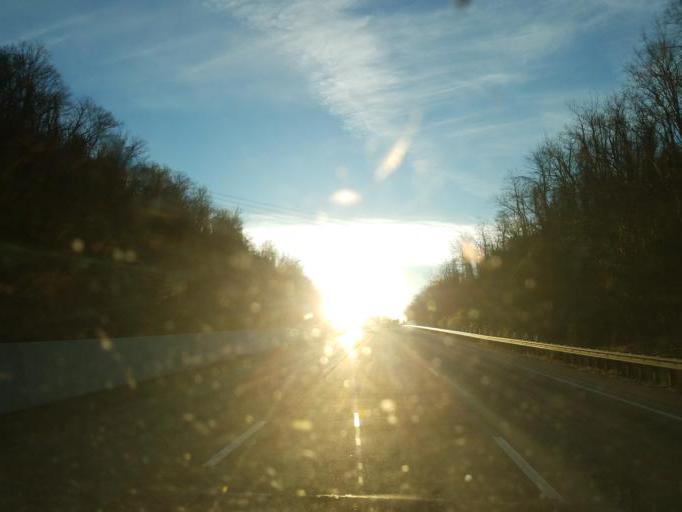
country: US
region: Ohio
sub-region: Belmont County
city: Wolfhurst
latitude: 40.0654
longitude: -80.8273
